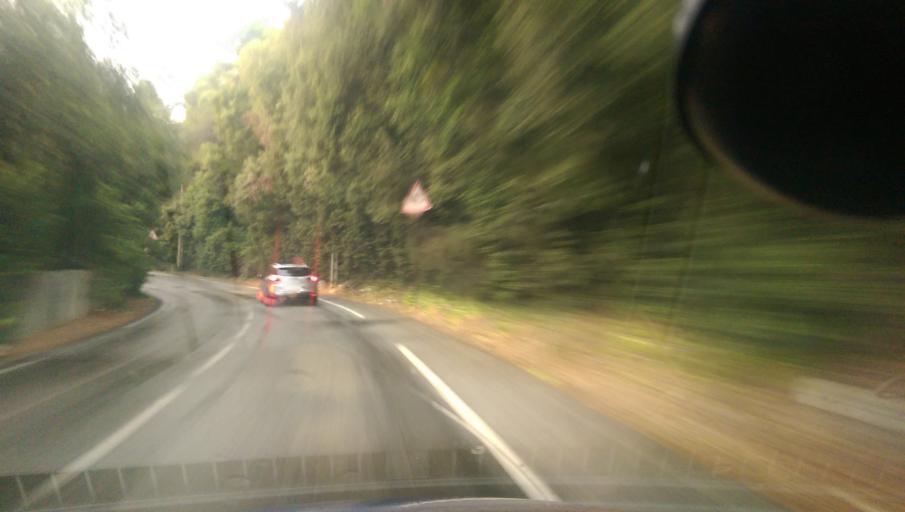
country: FR
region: Provence-Alpes-Cote d'Azur
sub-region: Departement des Alpes-Maritimes
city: Grasse
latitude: 43.6684
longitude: 6.9277
